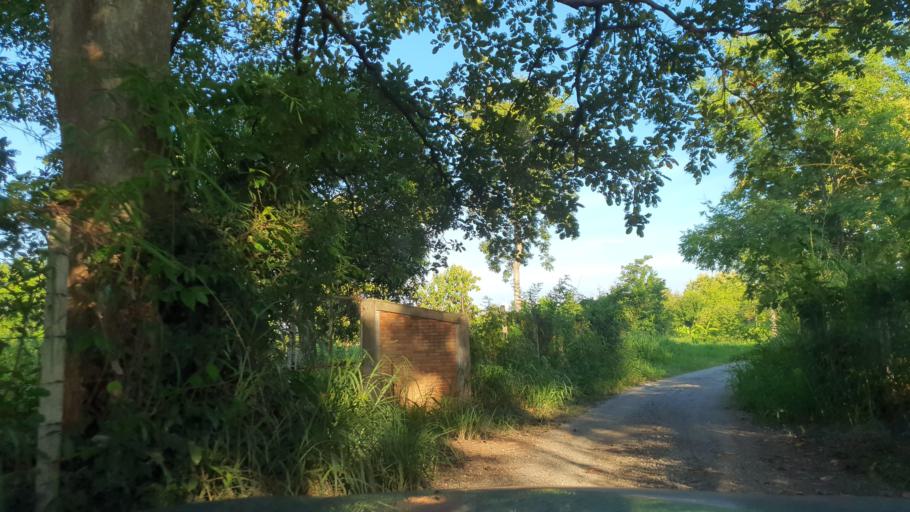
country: TH
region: Chiang Mai
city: Hang Dong
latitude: 18.6818
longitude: 98.8911
